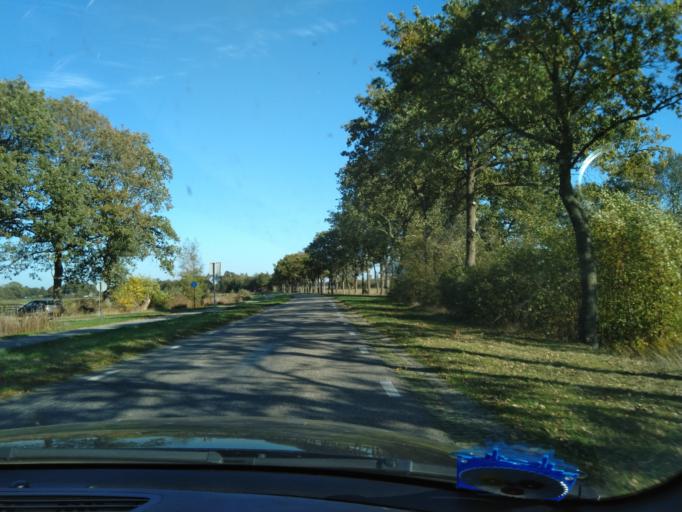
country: NL
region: Drenthe
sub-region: Gemeente Aa en Hunze
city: Anloo
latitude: 53.0265
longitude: 6.6526
